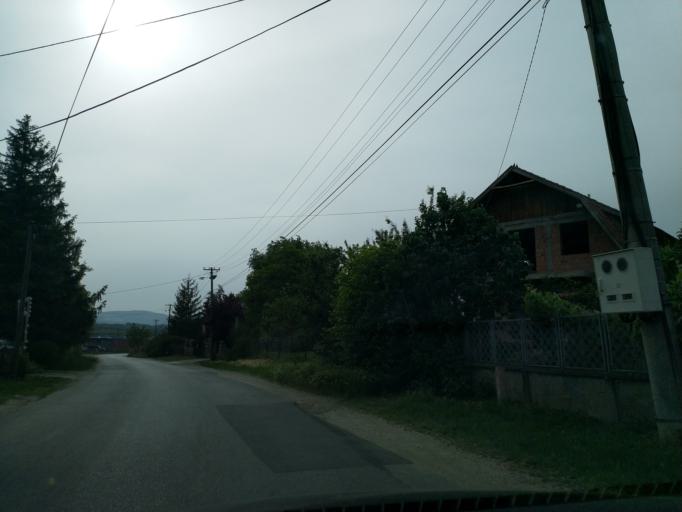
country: RS
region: Central Serbia
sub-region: Pomoravski Okrug
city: Jagodina
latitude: 43.9704
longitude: 21.2261
